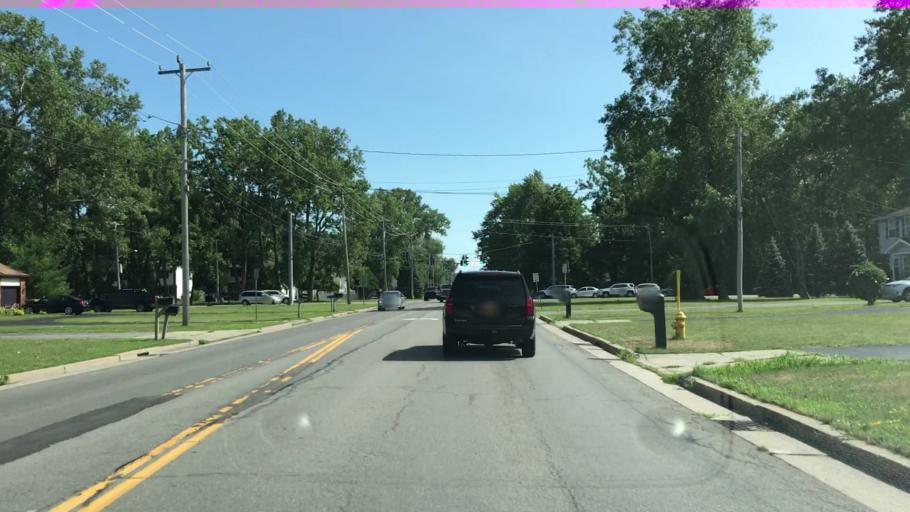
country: US
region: New York
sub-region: Erie County
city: Depew
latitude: 42.8933
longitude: -78.7086
